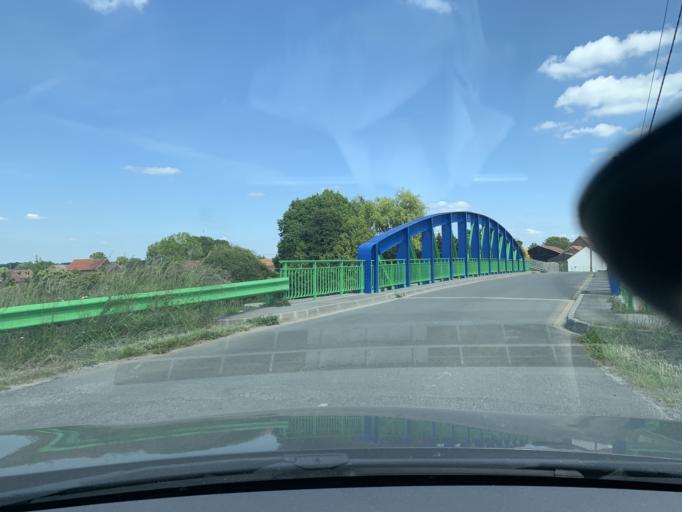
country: FR
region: Nord-Pas-de-Calais
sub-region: Departement du Pas-de-Calais
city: Marquion
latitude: 50.2352
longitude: 3.0921
